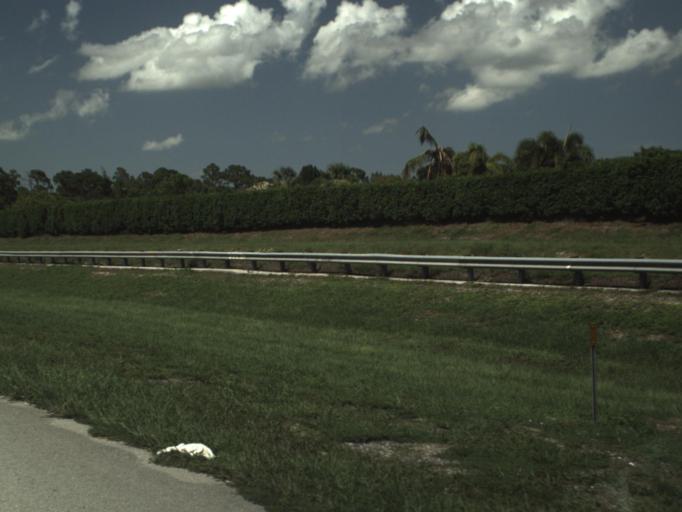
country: US
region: Florida
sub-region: Palm Beach County
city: Wellington
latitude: 26.6075
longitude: -80.2051
